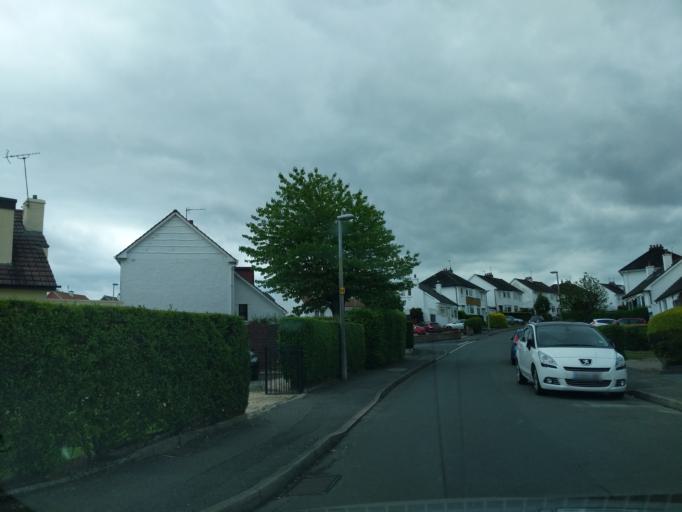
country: GB
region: Scotland
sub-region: Edinburgh
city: Colinton
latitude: 55.9697
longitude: -3.2665
